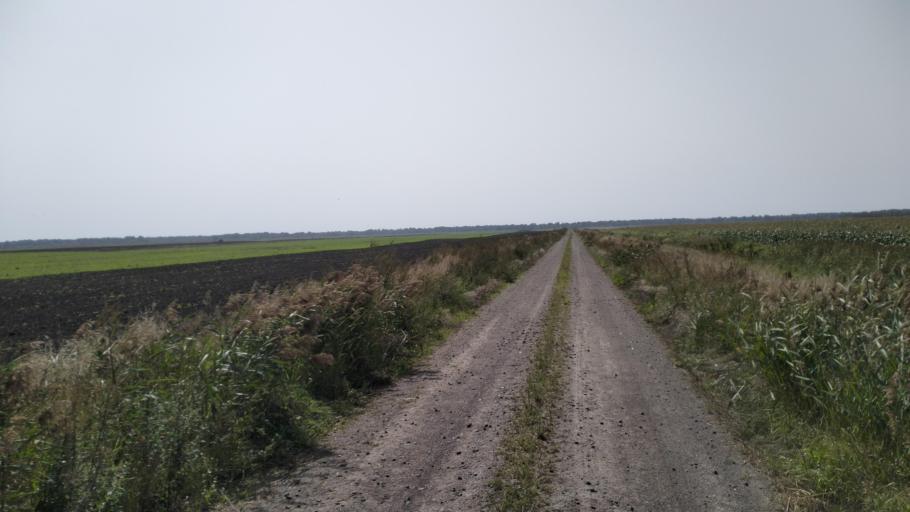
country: BY
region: Brest
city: Davyd-Haradok
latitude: 51.9874
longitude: 27.1641
